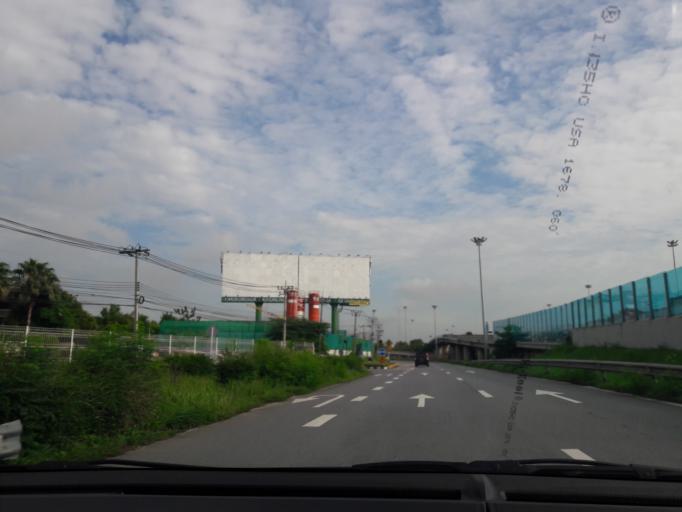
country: TH
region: Bangkok
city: Khan Na Yao
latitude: 13.8249
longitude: 100.6740
